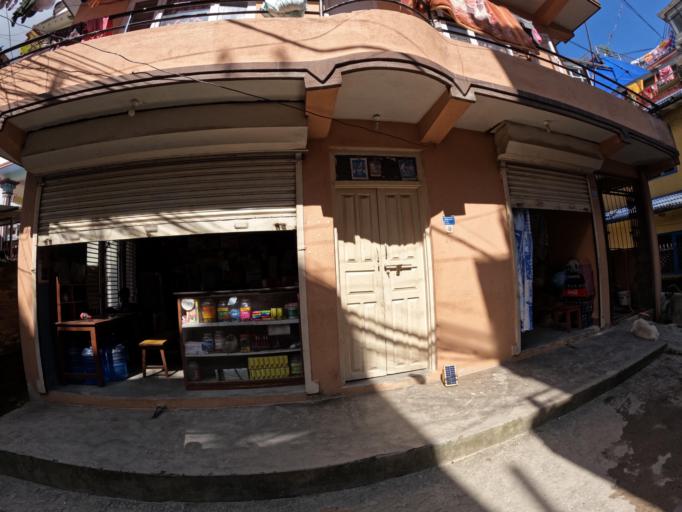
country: NP
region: Central Region
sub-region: Bagmati Zone
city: Kathmandu
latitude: 27.7485
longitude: 85.3326
